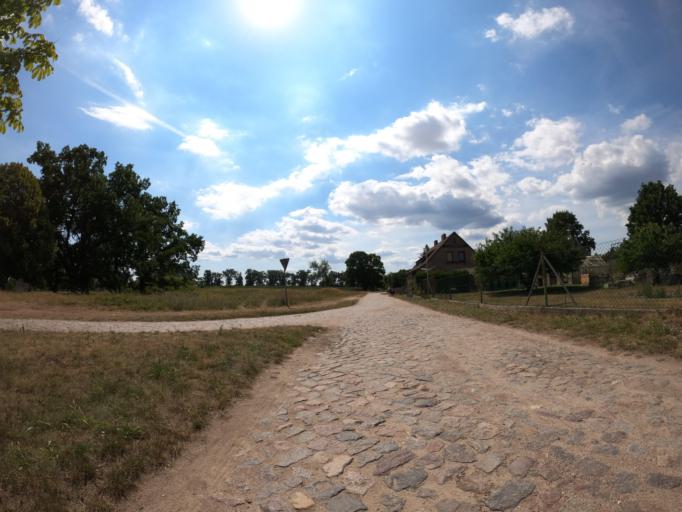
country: DE
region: Brandenburg
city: Mittenwalde
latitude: 53.2975
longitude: 13.5659
